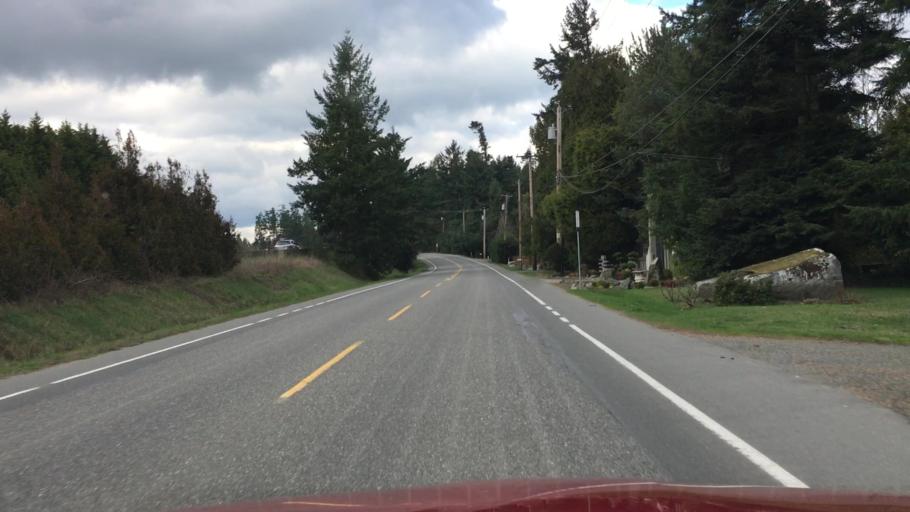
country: CA
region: British Columbia
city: North Saanich
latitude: 48.6038
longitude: -123.3960
